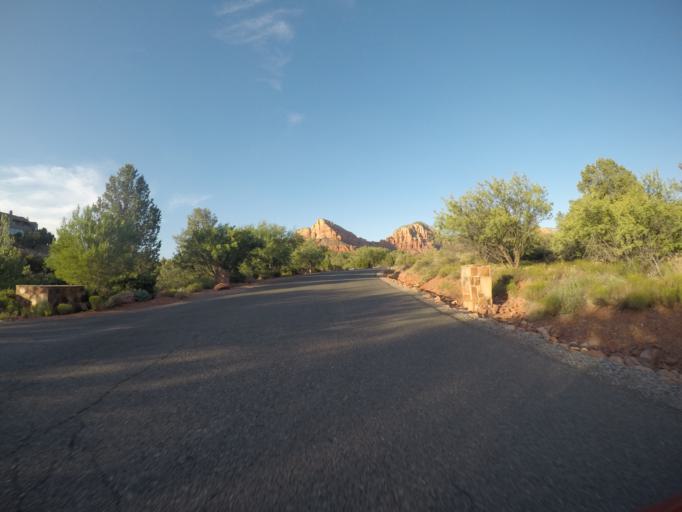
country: US
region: Arizona
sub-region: Yavapai County
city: West Sedona
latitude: 34.8268
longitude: -111.7810
